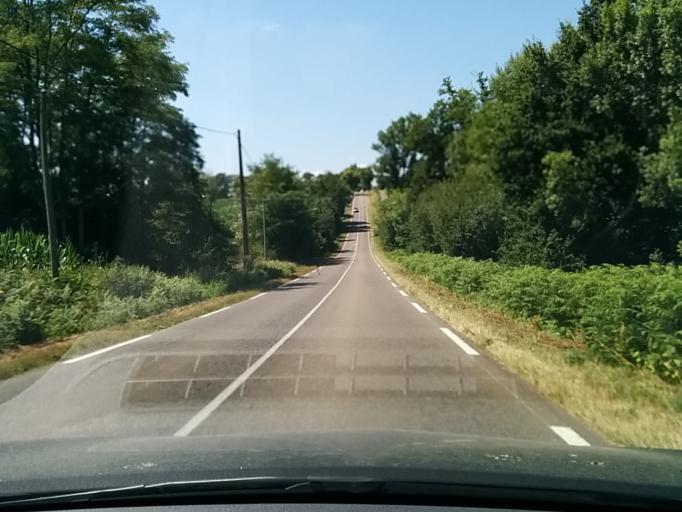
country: FR
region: Midi-Pyrenees
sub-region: Departement du Gers
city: Nogaro
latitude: 43.7590
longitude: -0.1042
